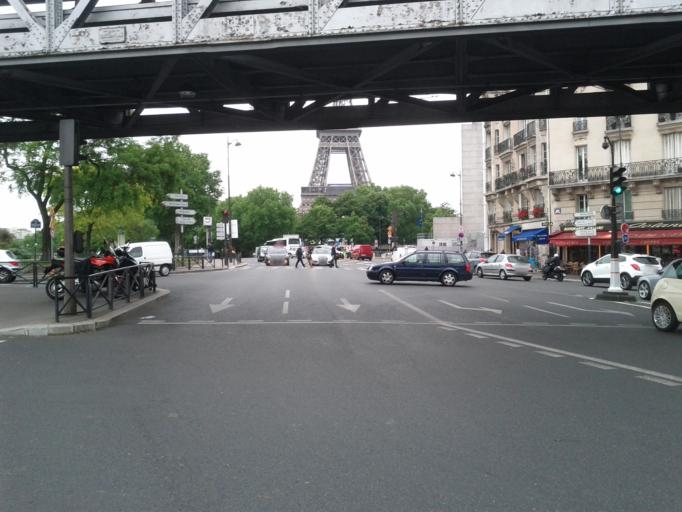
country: FR
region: Ile-de-France
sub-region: Departement des Hauts-de-Seine
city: Vanves
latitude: 48.8545
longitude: 2.2885
